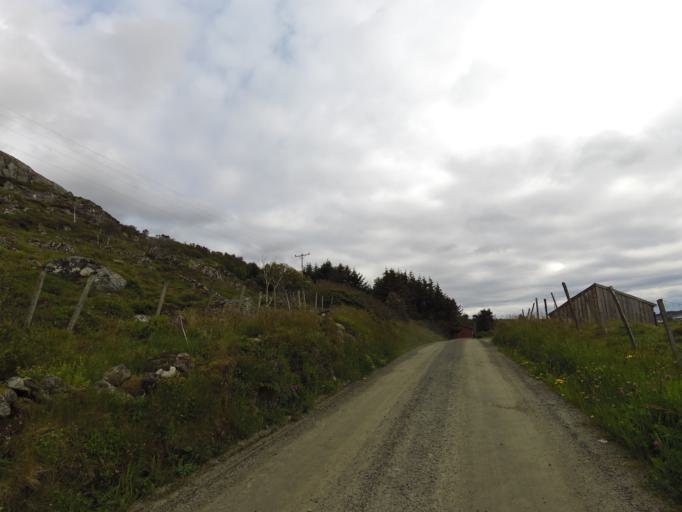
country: NO
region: Vest-Agder
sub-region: Farsund
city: Vestbygd
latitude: 58.1444
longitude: 6.6134
